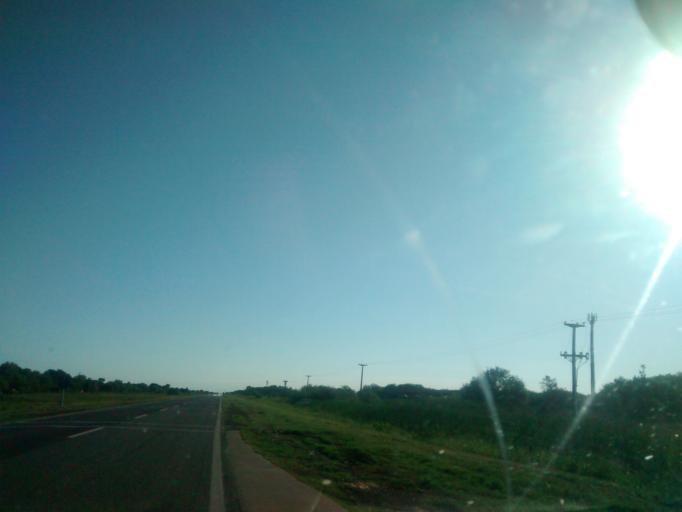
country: AR
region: Chaco
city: Fontana
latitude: -27.4745
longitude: -59.0553
